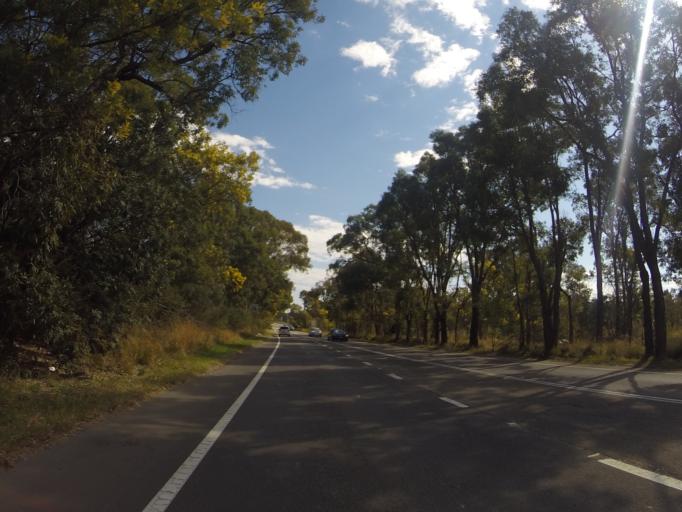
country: AU
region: New South Wales
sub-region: Liverpool
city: East Hills
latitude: -33.9659
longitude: 150.9698
